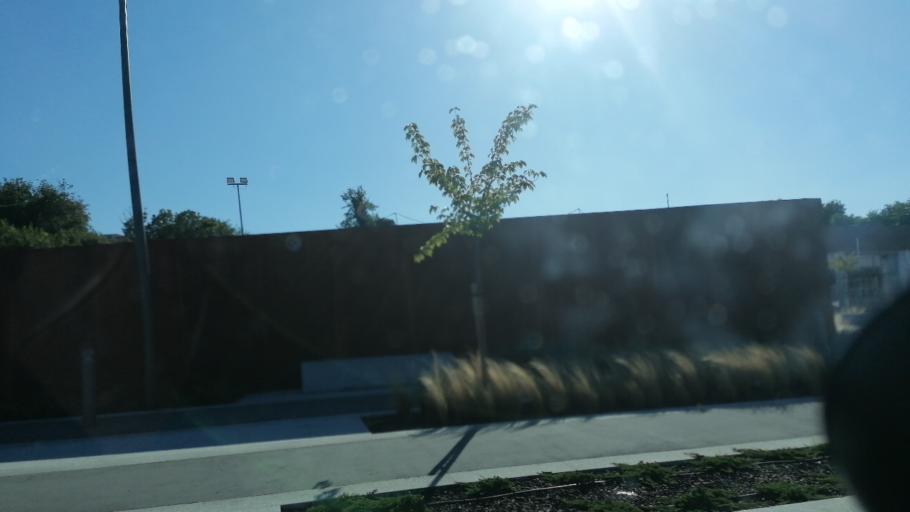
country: PT
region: Porto
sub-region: Santo Tirso
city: Santo Tirso
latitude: 41.3499
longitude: -8.4758
